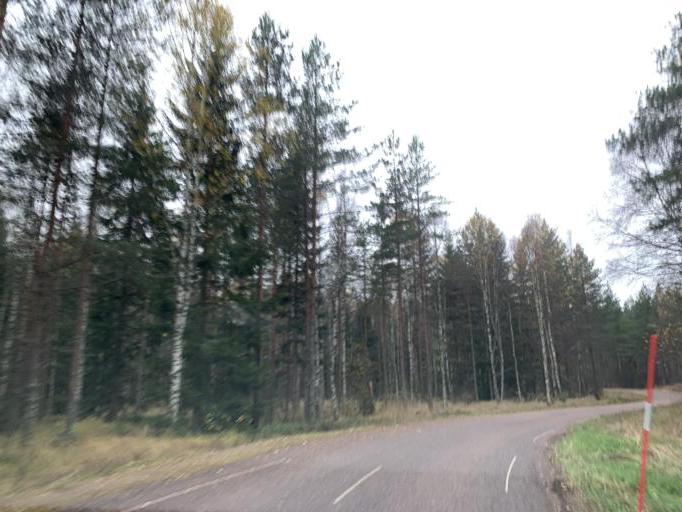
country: SE
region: Vaestmanland
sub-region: Surahammars Kommun
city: Surahammar
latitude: 59.6589
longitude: 16.0799
